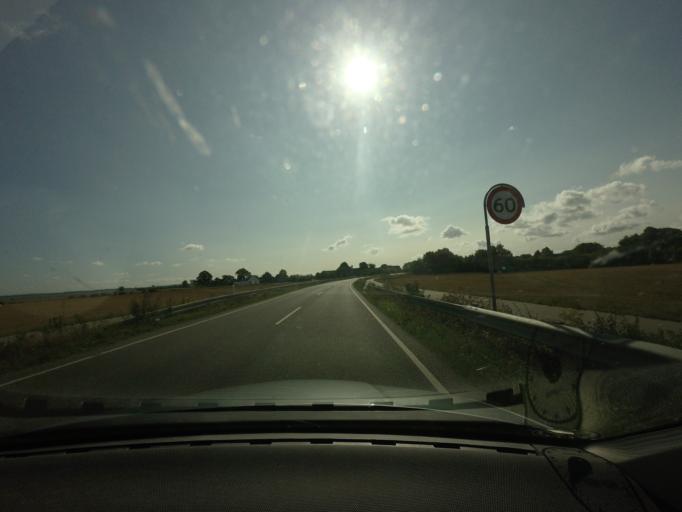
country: DK
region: Zealand
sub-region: Vordingborg Kommune
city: Stege
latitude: 54.9774
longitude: 12.1907
